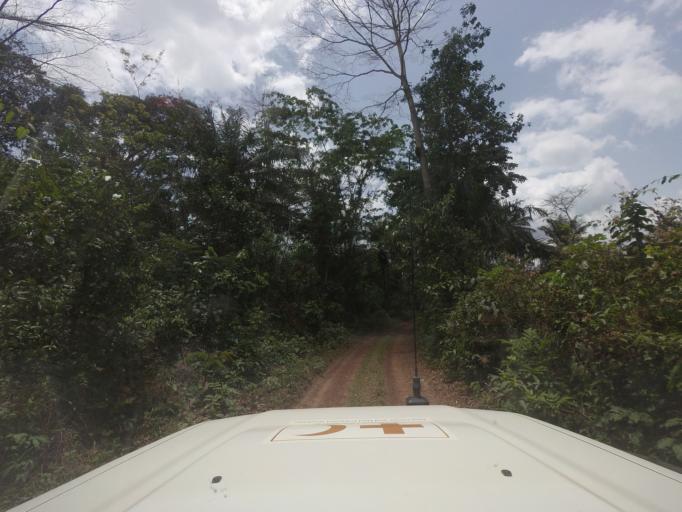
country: LR
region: Bong
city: Gbarnga
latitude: 7.1899
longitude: -9.1988
